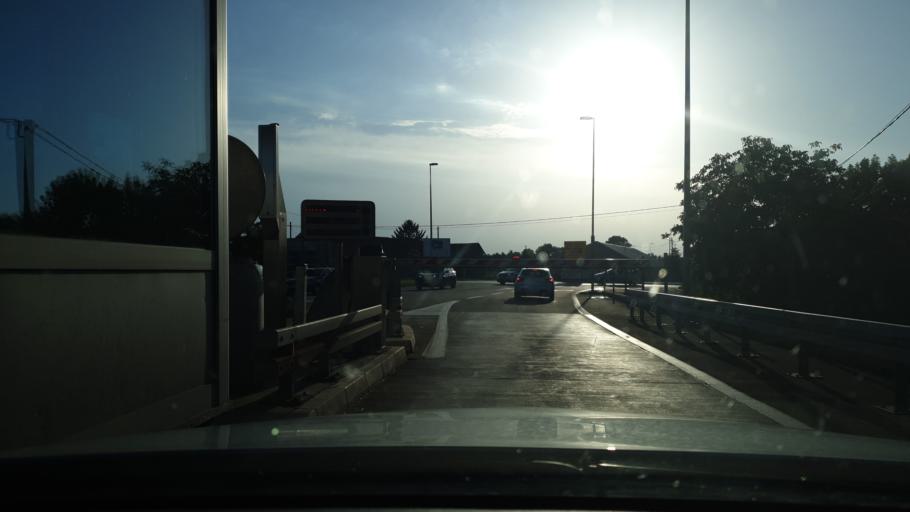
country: RS
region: Central Serbia
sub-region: Podunavski Okrug
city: Velika Plana
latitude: 44.3392
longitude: 21.0800
